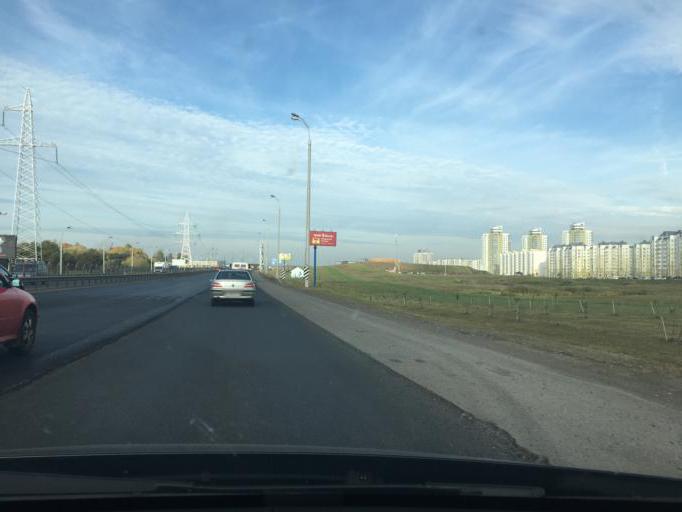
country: BY
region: Minsk
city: Zhdanovichy
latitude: 53.9236
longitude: 27.4163
